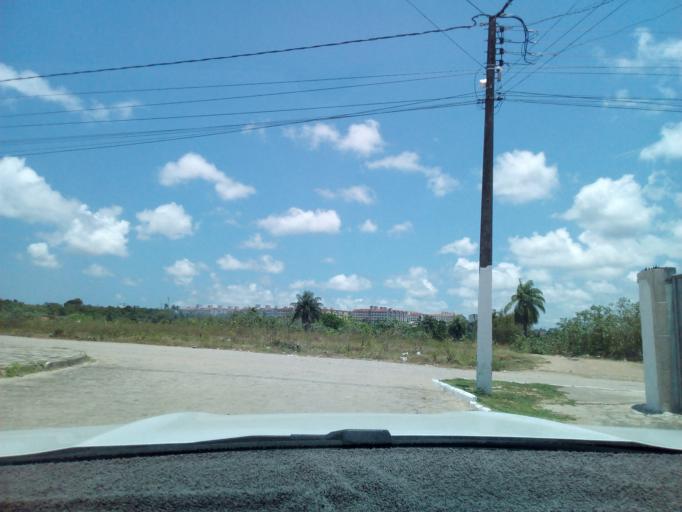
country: BR
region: Paraiba
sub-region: Bayeux
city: Bayeux
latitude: -7.1856
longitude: -34.8885
